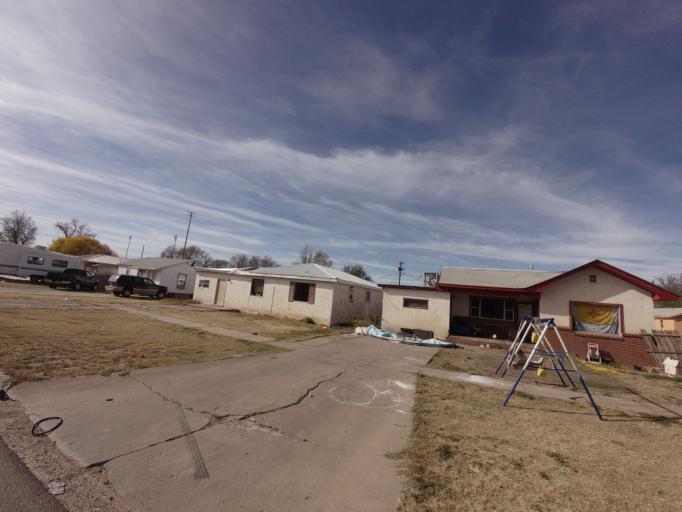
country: US
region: New Mexico
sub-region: Curry County
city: Clovis
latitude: 34.4053
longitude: -103.1890
